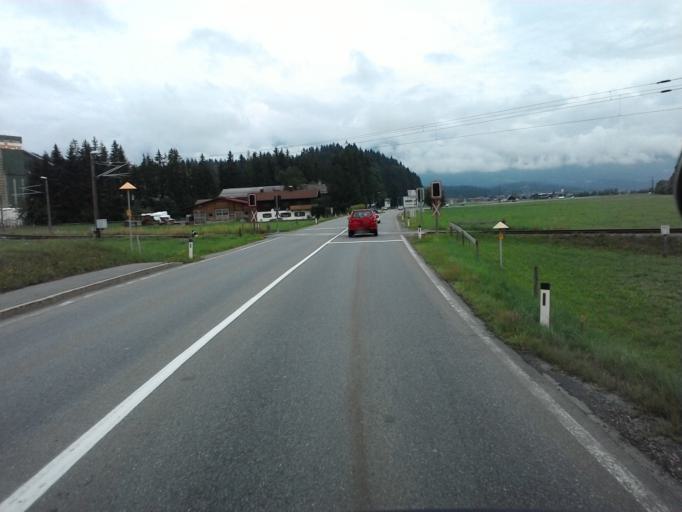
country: AT
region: Tyrol
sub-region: Politischer Bezirk Kitzbuhel
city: Oberndorf in Tirol
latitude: 47.4840
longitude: 12.3795
